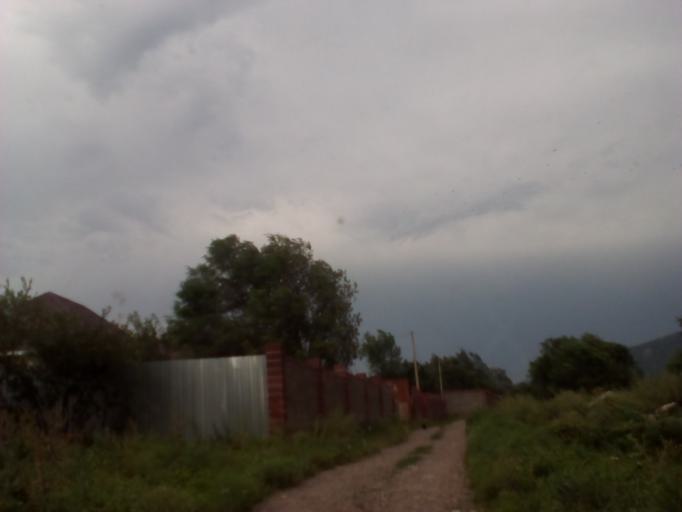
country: KZ
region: Almaty Oblysy
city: Burunday
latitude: 43.1581
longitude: 76.3977
